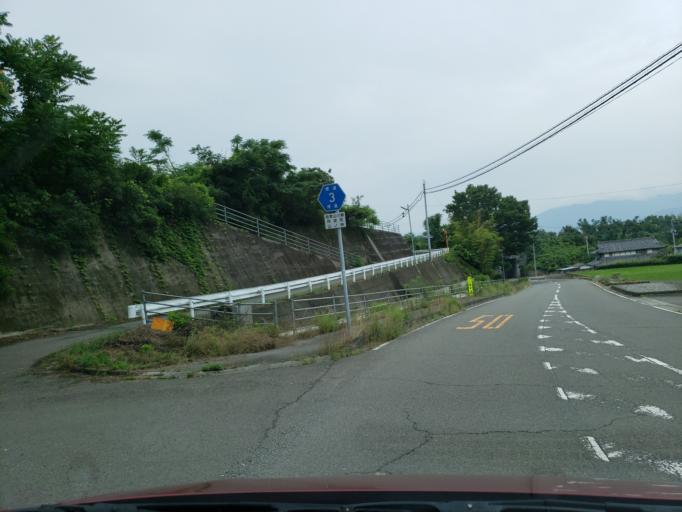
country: JP
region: Tokushima
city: Wakimachi
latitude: 34.1007
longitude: 134.2262
